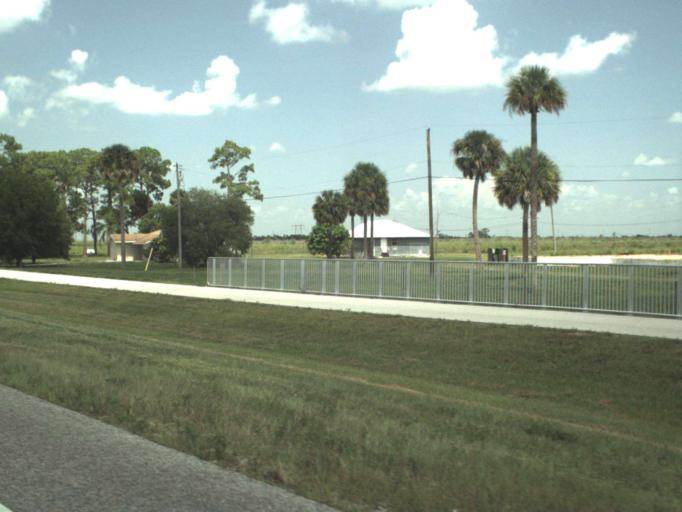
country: US
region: Florida
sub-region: Saint Lucie County
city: Fort Pierce South
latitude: 27.3754
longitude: -80.4909
